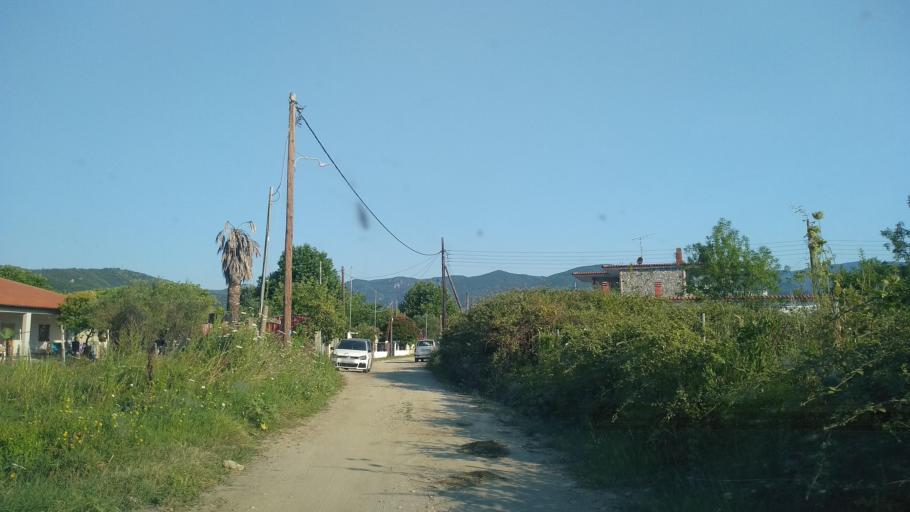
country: GR
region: Central Macedonia
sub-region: Nomos Thessalonikis
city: Stavros
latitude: 40.6850
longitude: 23.6869
